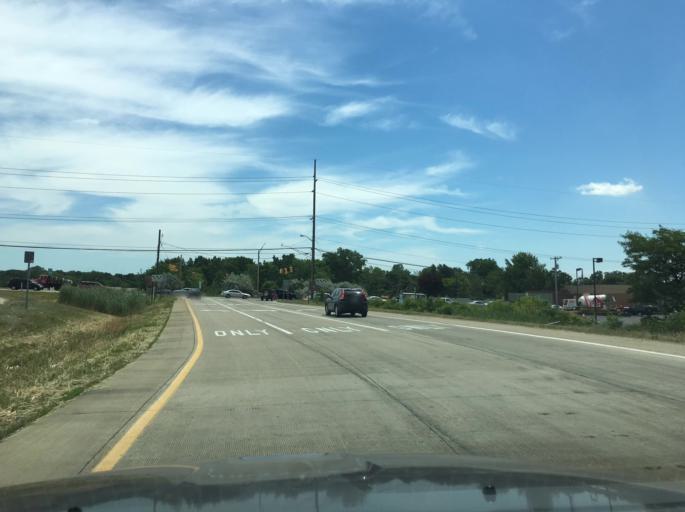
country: US
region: Michigan
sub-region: Oakland County
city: Troy
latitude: 42.6266
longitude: -83.1325
